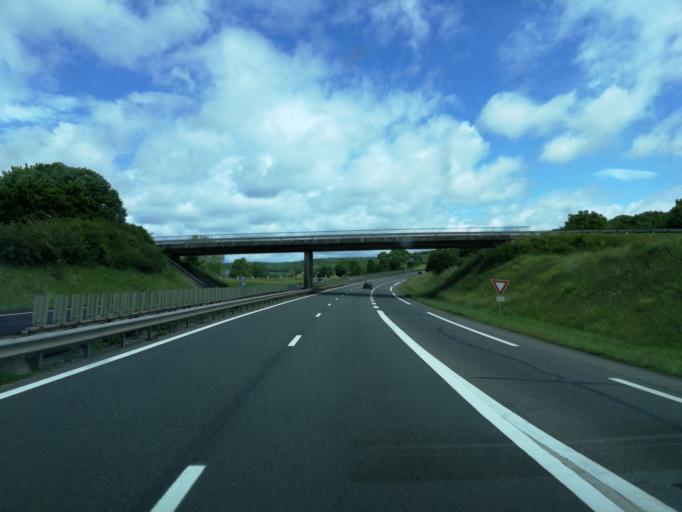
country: FR
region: Haute-Normandie
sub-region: Departement de l'Eure
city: Gravigny
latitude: 49.0590
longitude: 1.1746
